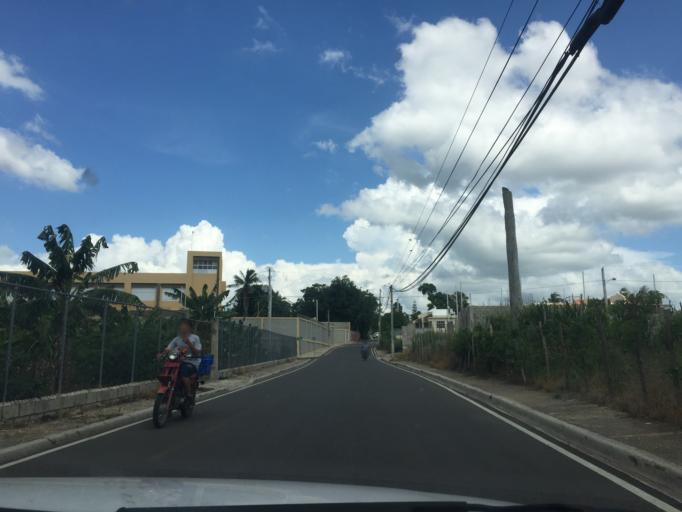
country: DO
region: Santiago
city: Licey al Medio
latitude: 19.3790
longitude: -70.6016
